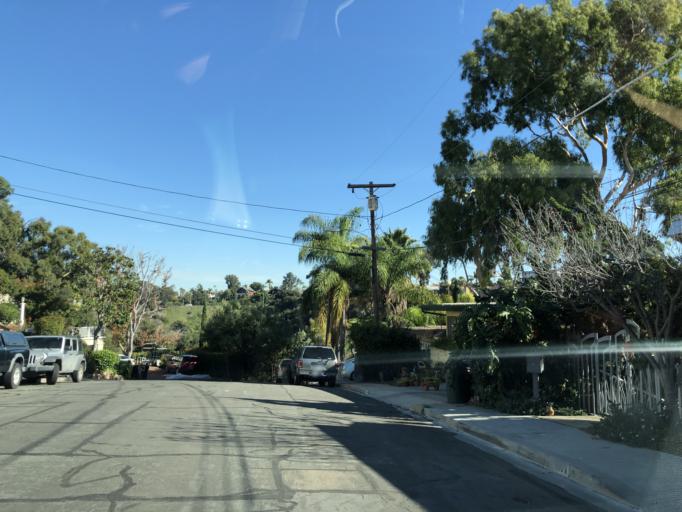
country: US
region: California
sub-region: San Diego County
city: San Diego
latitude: 32.7329
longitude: -117.1335
